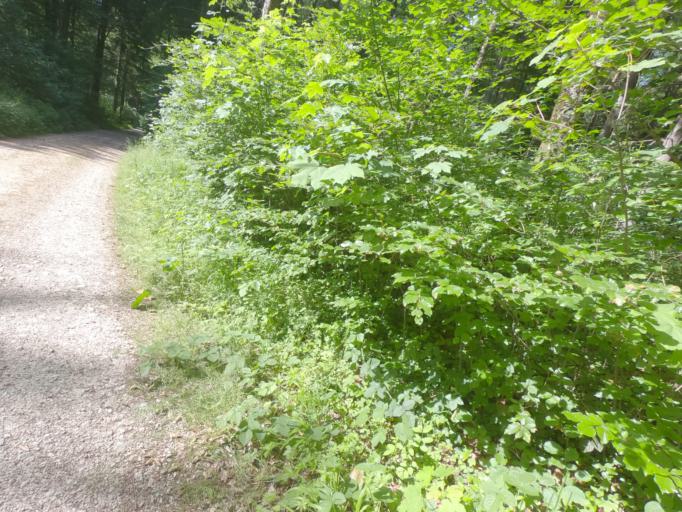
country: CH
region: Solothurn
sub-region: Bezirk Solothurn
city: Solothurn
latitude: 47.2293
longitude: 7.5364
